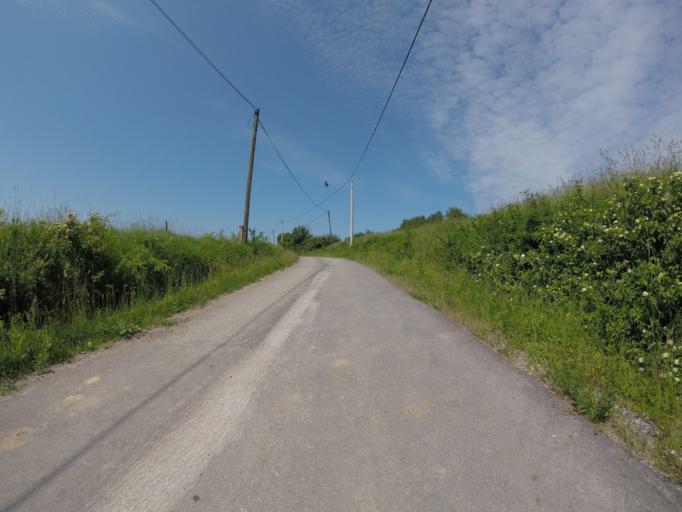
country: HR
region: Zagrebacka
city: Lukavec
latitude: 45.5841
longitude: 15.9993
